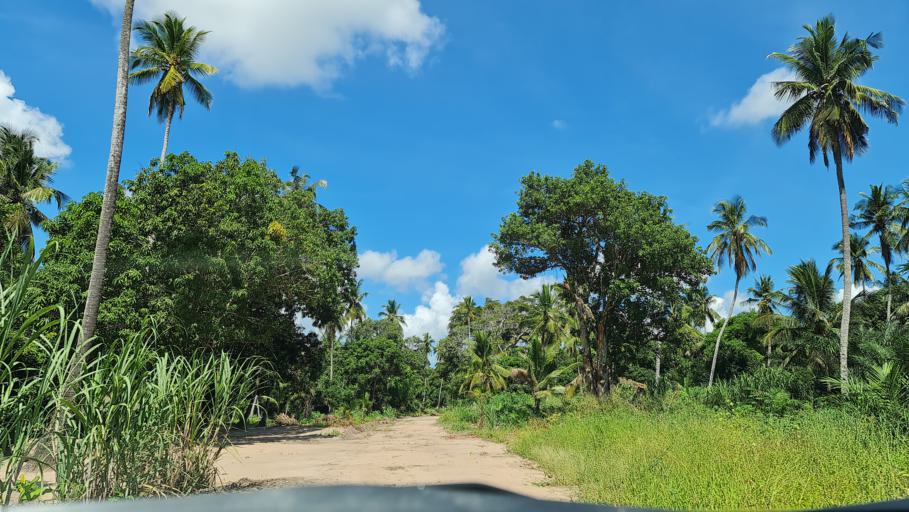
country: MZ
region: Zambezia
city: Quelimane
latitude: -17.3844
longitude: 37.5277
